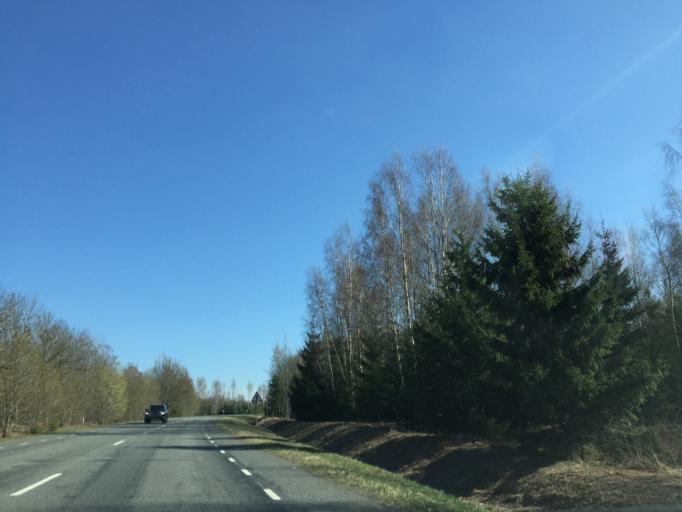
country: EE
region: Viljandimaa
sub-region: Viiratsi vald
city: Viiratsi
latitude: 58.2744
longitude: 25.6103
